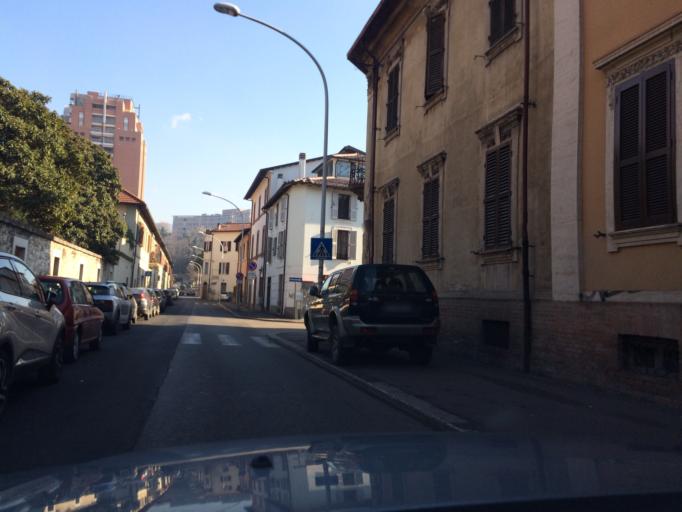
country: IT
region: Umbria
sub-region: Provincia di Terni
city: Terni
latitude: 42.5592
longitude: 12.6513
